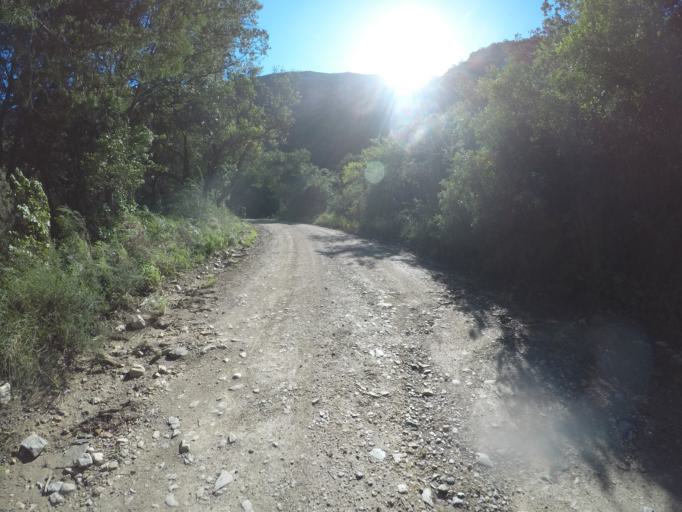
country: ZA
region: Eastern Cape
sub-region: Cacadu District Municipality
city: Kareedouw
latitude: -33.6601
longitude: 24.5350
